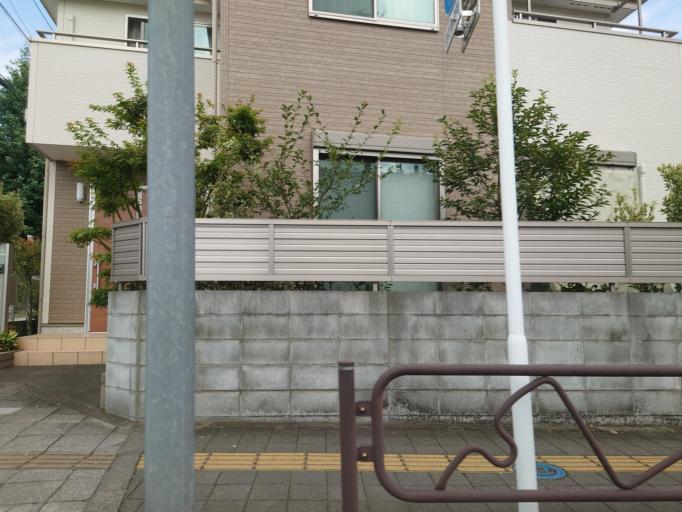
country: JP
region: Tokyo
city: Fussa
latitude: 35.7629
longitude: 139.3174
